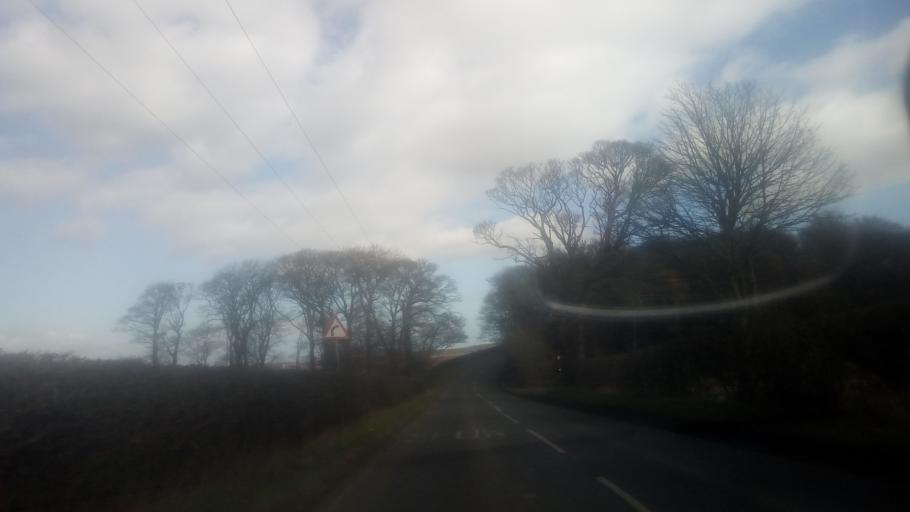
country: GB
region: Scotland
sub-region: East Lothian
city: Ormiston
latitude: 55.9009
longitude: -2.9472
